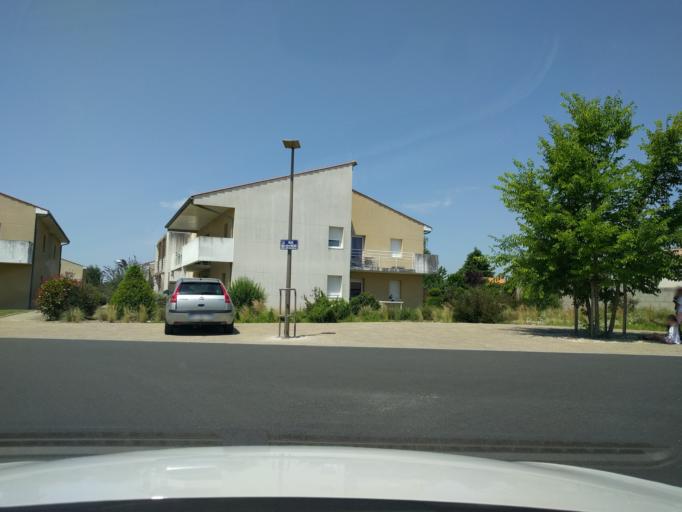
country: FR
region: Poitou-Charentes
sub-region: Departement des Deux-Sevres
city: Niort
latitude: 46.3458
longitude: -0.4588
